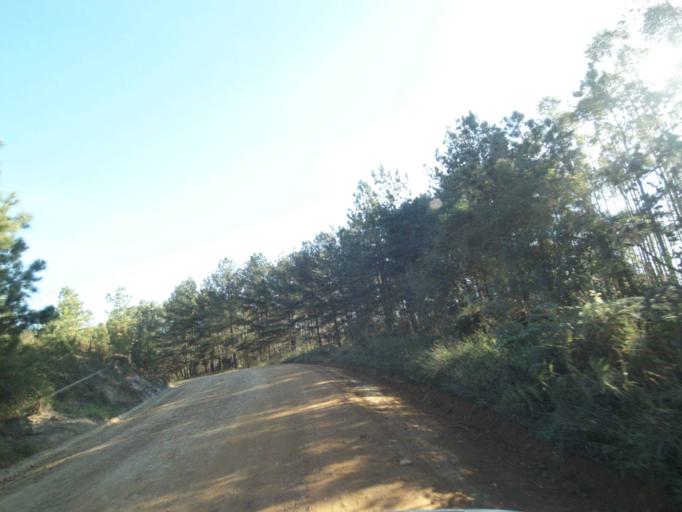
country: BR
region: Parana
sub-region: Tibagi
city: Tibagi
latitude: -24.5361
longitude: -50.5266
